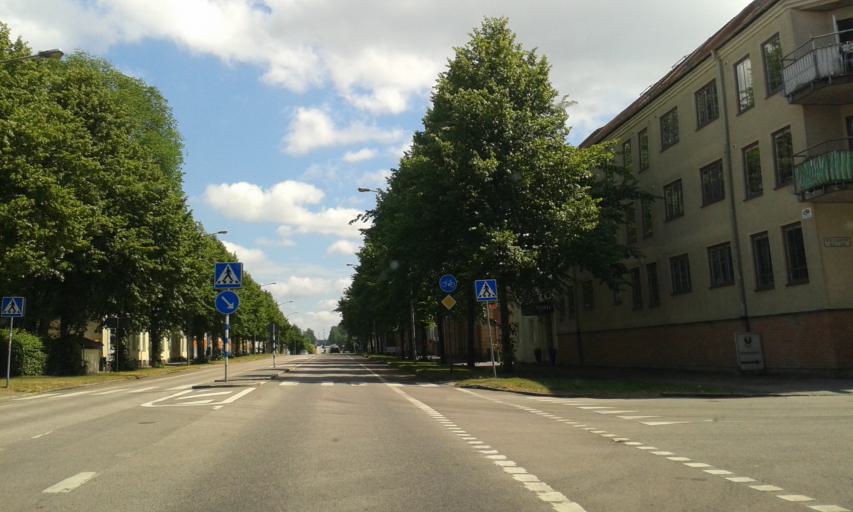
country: SE
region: Kronoberg
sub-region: Vaxjo Kommun
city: Vaexjoe
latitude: 56.8817
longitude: 14.8049
